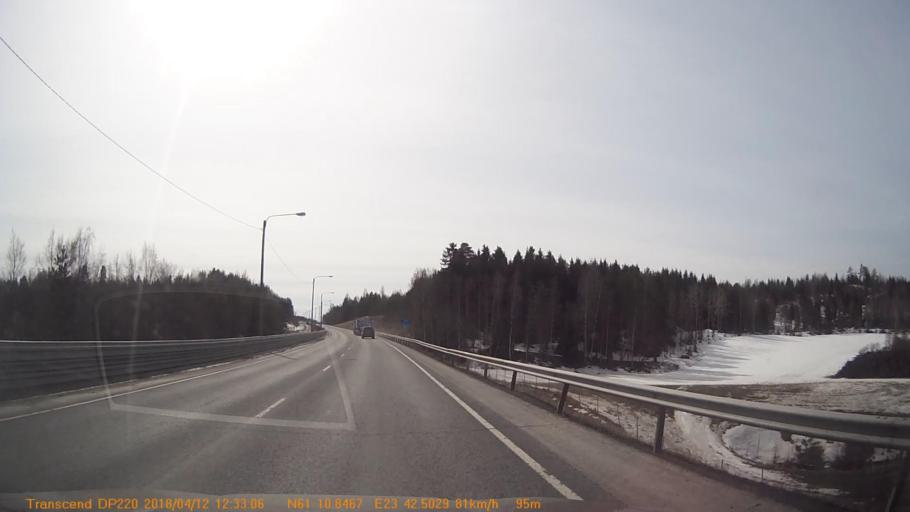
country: FI
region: Pirkanmaa
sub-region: Etelae-Pirkanmaa
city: Kylmaekoski
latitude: 61.1806
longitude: 23.7082
